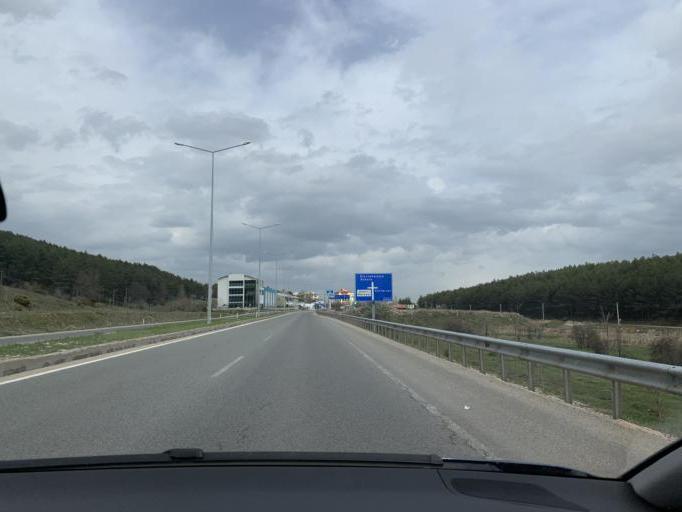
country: TR
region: Bolu
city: Gerede
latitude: 40.7992
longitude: 32.1782
